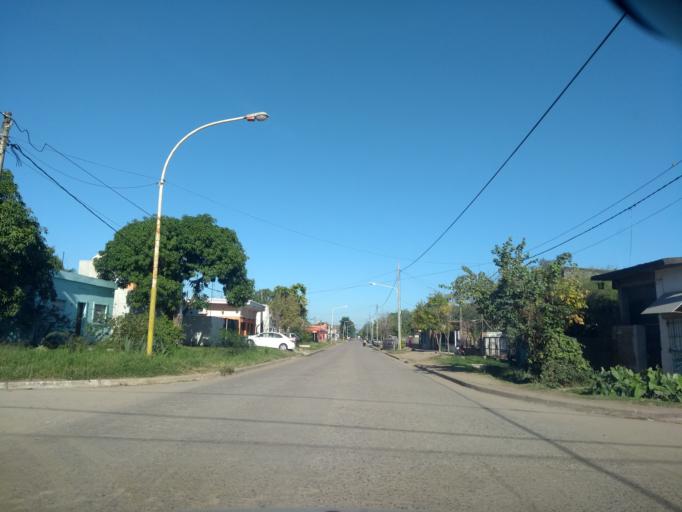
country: AR
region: Chaco
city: Barranqueras
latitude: -27.4842
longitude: -58.9288
